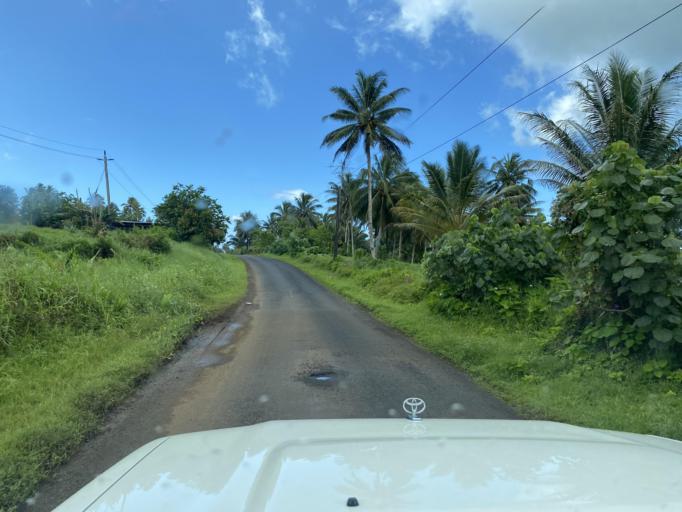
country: WS
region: Va`a-o-Fonoti
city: Samamea
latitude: -13.9797
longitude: -171.5881
